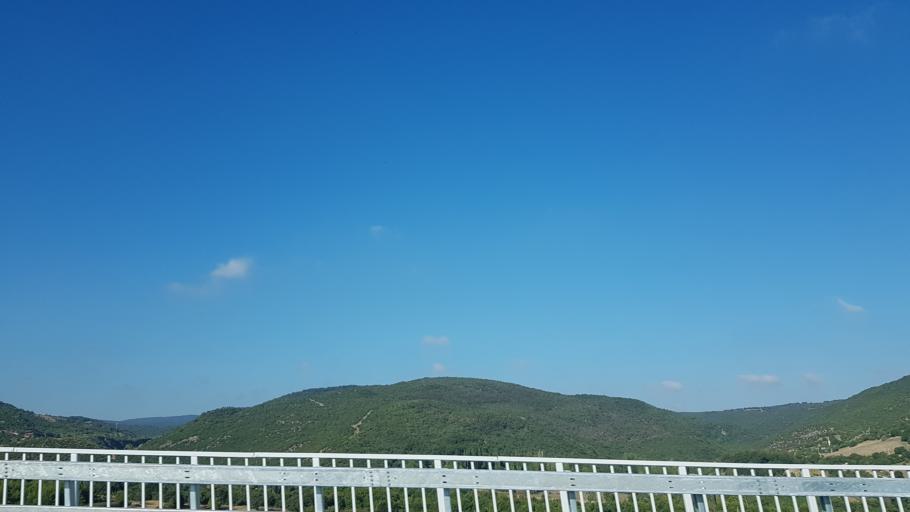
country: TR
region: Balikesir
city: Ertugrul
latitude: 39.5725
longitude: 27.7007
